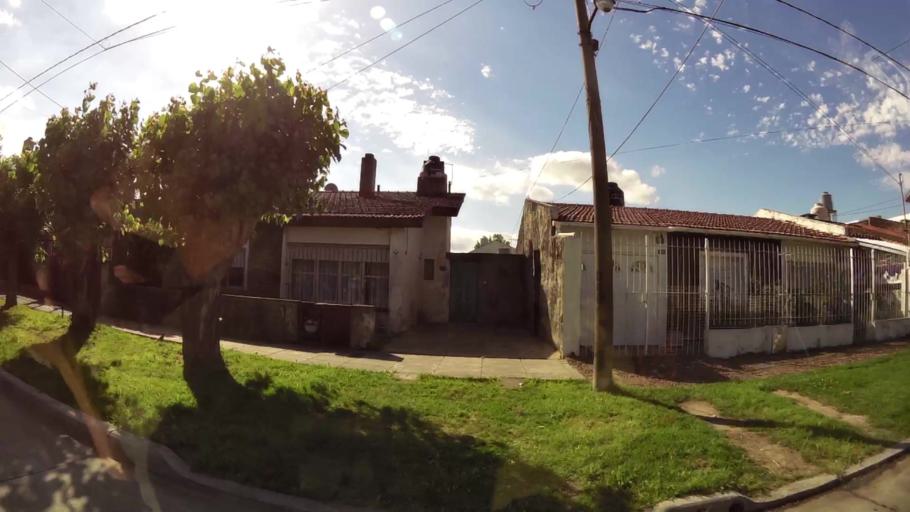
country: AR
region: Buenos Aires
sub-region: Partido de Moron
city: Moron
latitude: -34.6615
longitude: -58.5933
